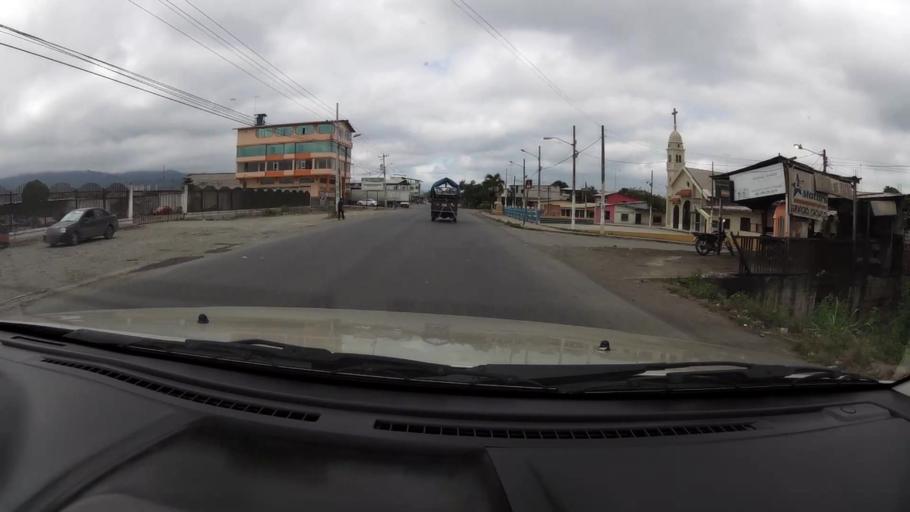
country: EC
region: Guayas
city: Naranjal
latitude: -2.6800
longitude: -79.6197
